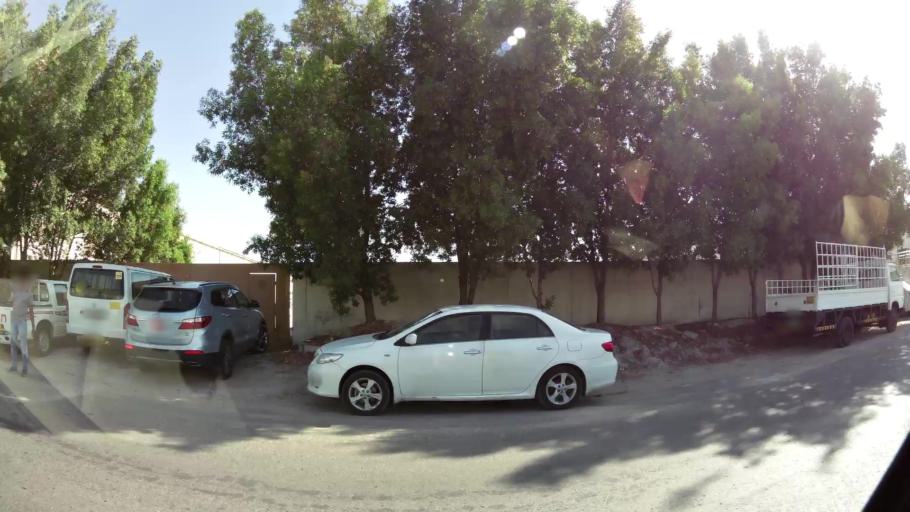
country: AE
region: Dubai
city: Dubai
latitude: 25.1299
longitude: 55.2282
